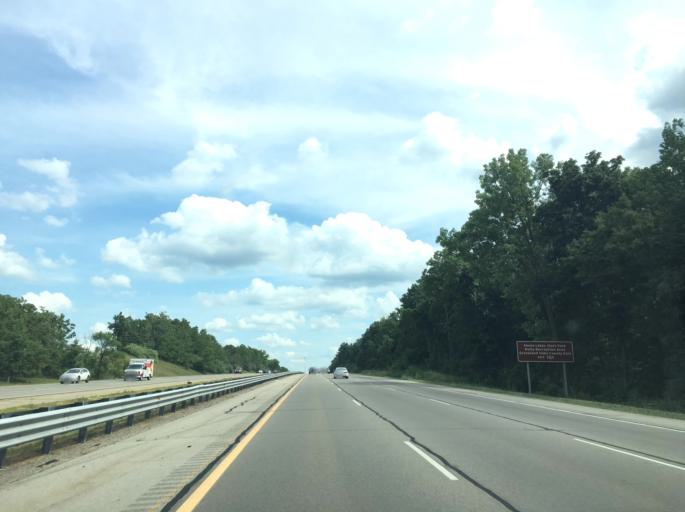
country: US
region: Michigan
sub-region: Oakland County
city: Holly
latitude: 42.8318
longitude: -83.5771
